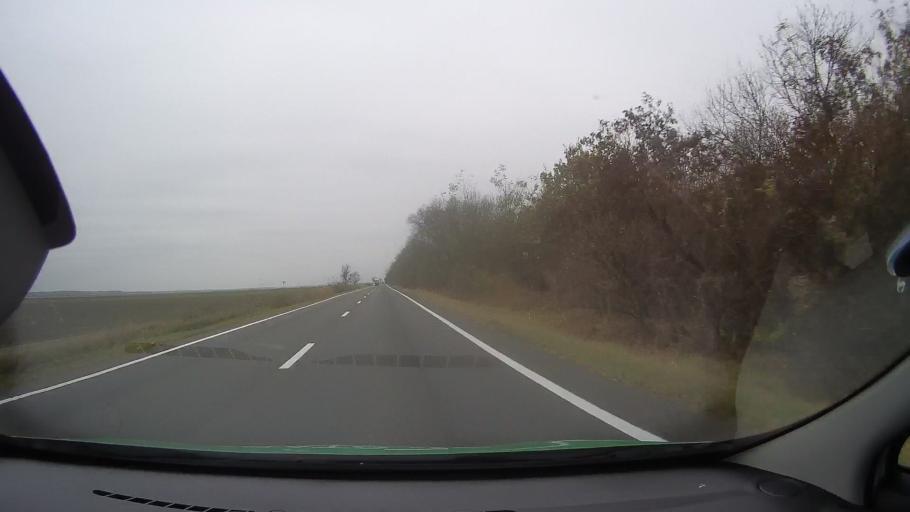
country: RO
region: Ialomita
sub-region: Comuna Mihail Kogalniceanu
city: Mihail Kogalniceanu
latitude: 44.6711
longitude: 27.7556
